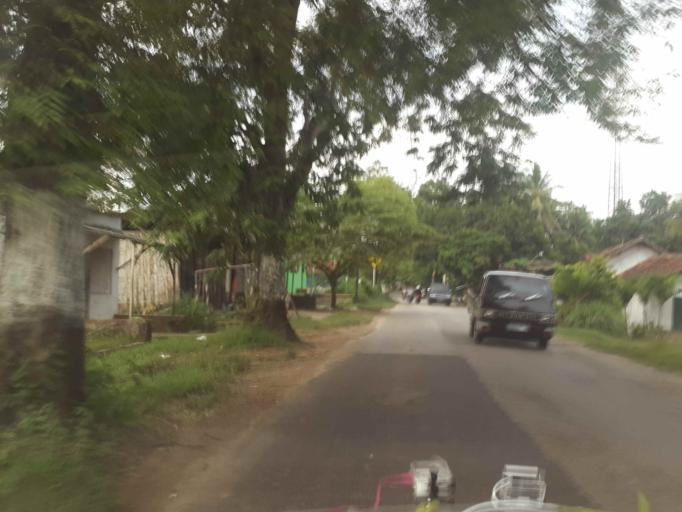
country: ID
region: East Java
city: Ganjur
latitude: -6.9843
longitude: 113.8593
